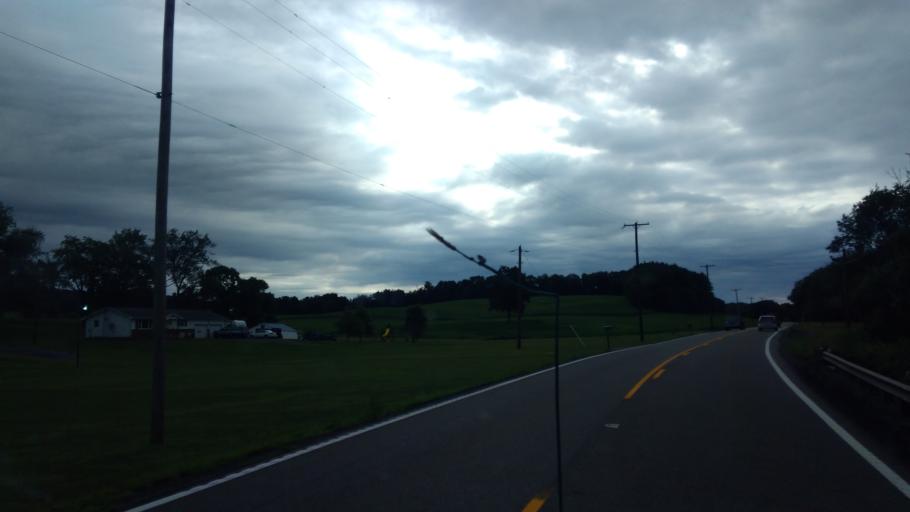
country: US
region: Ohio
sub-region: Columbiana County
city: Lisbon
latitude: 40.7552
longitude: -80.9183
